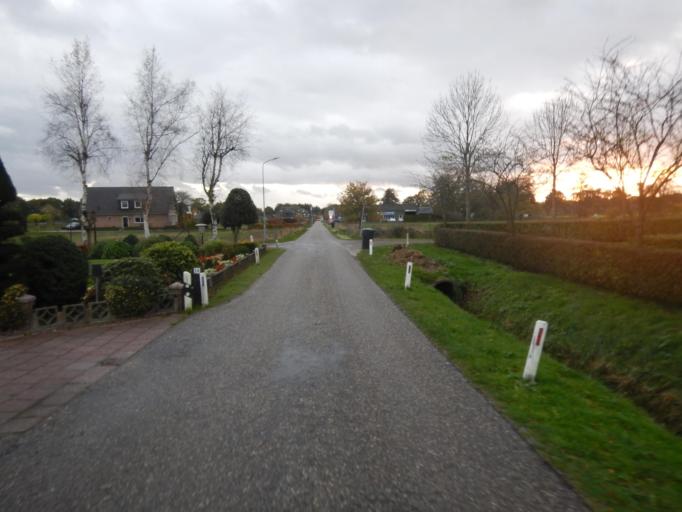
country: NL
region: Gelderland
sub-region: Gemeente Barneveld
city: Garderen
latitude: 52.2751
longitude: 5.7180
